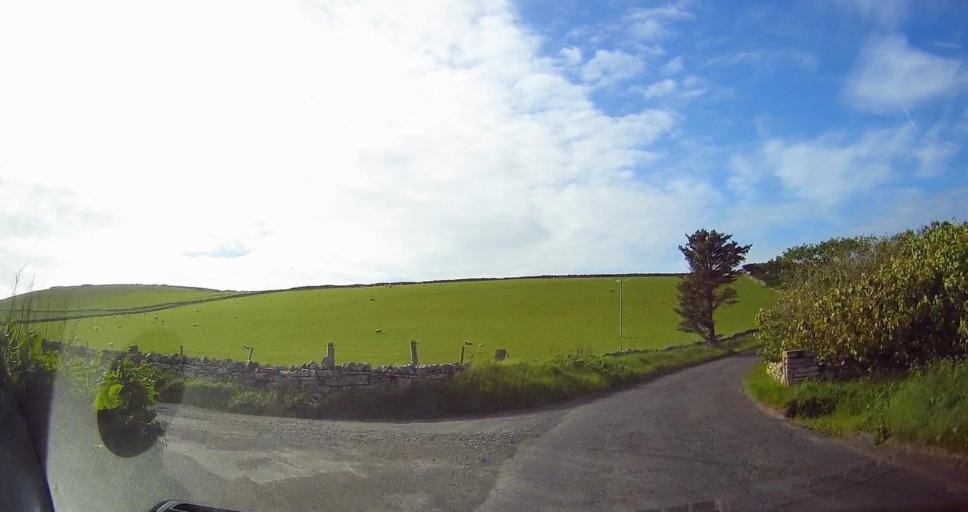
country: GB
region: Scotland
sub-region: Orkney Islands
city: Stromness
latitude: 58.7869
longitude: -3.2598
